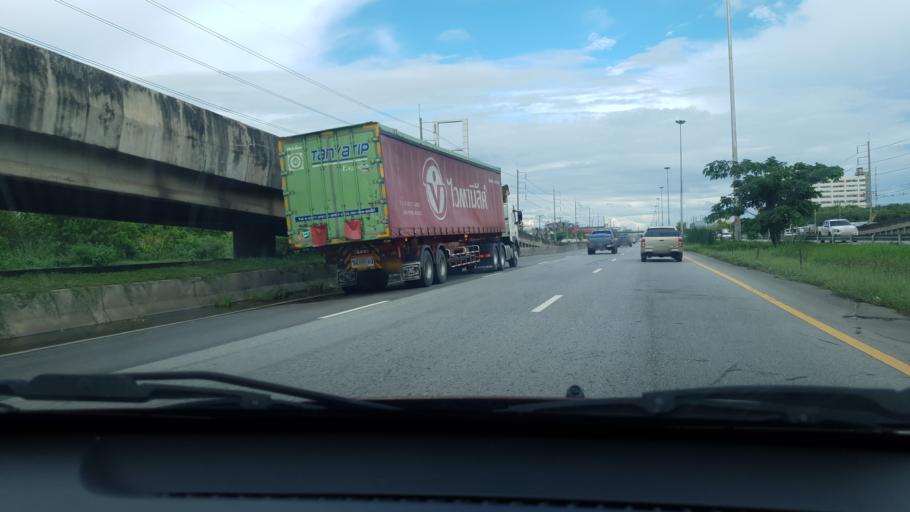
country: TH
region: Samut Sakhon
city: Samut Sakhon
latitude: 13.5379
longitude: 100.2240
